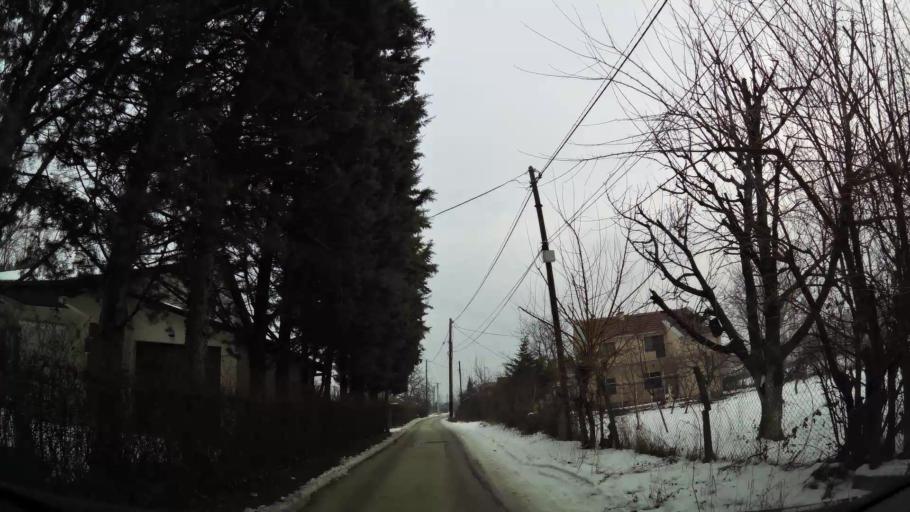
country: MK
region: Saraj
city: Saraj
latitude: 42.0493
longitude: 21.3593
